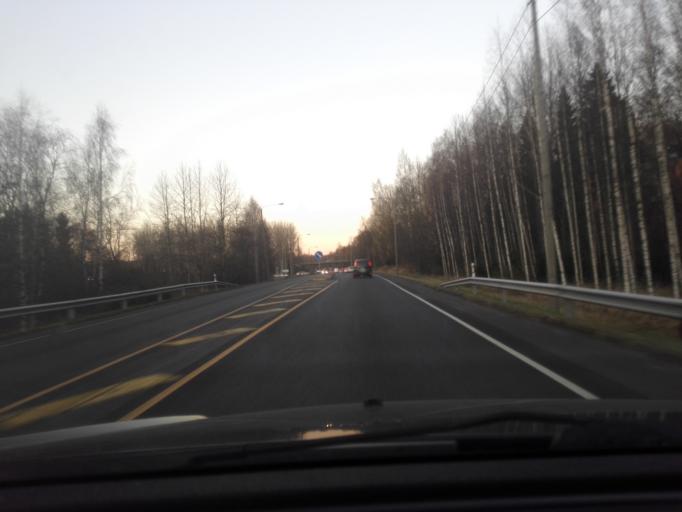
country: FI
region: Uusimaa
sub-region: Helsinki
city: Vantaa
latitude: 60.2772
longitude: 25.0978
